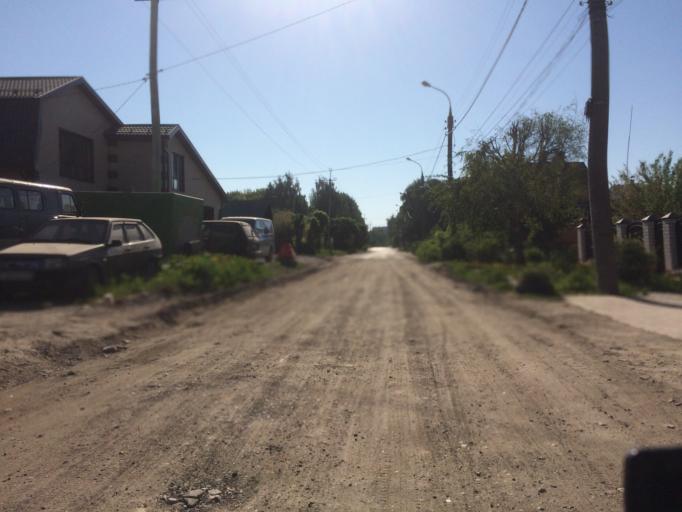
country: RU
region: Mariy-El
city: Medvedevo
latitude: 56.6478
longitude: 47.8428
